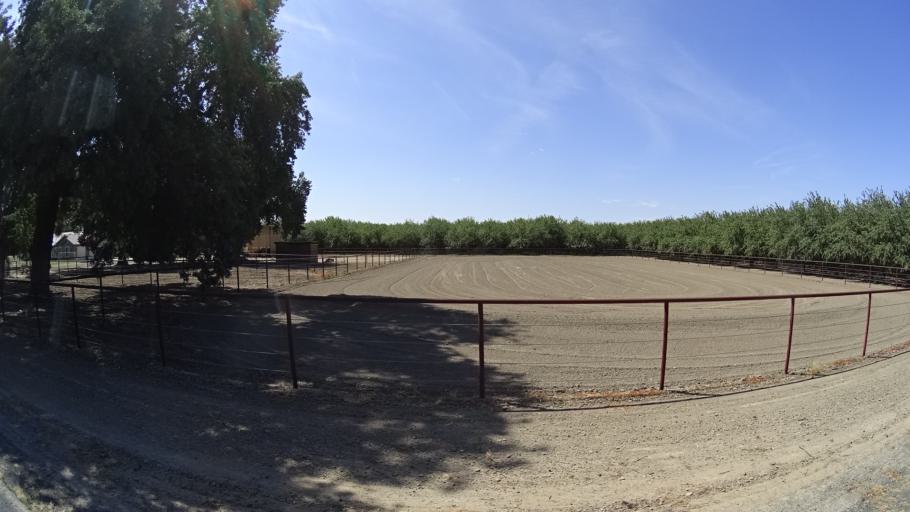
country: US
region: California
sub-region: Kings County
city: Lemoore
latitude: 36.2694
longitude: -119.7481
